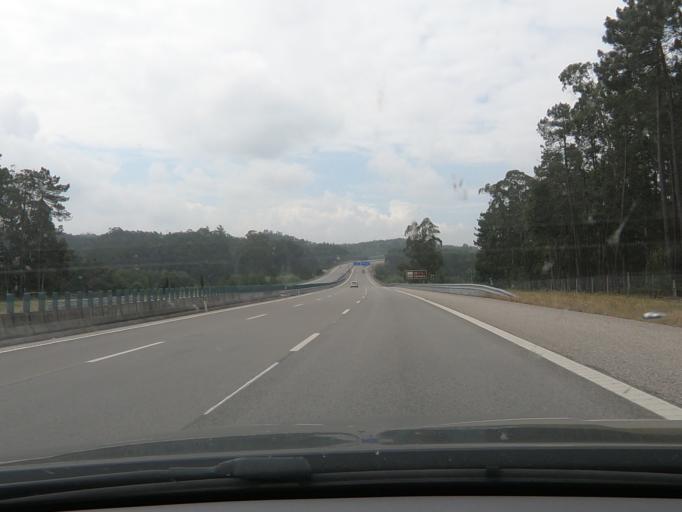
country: PT
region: Leiria
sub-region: Leiria
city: Souto da Carpalhosa
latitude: 39.8690
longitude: -8.8248
